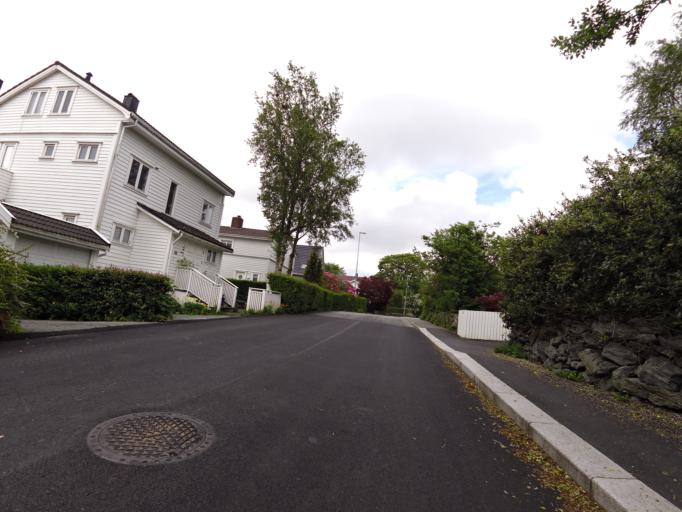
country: NO
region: Rogaland
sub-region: Stavanger
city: Stavanger
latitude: 58.9587
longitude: 5.7032
